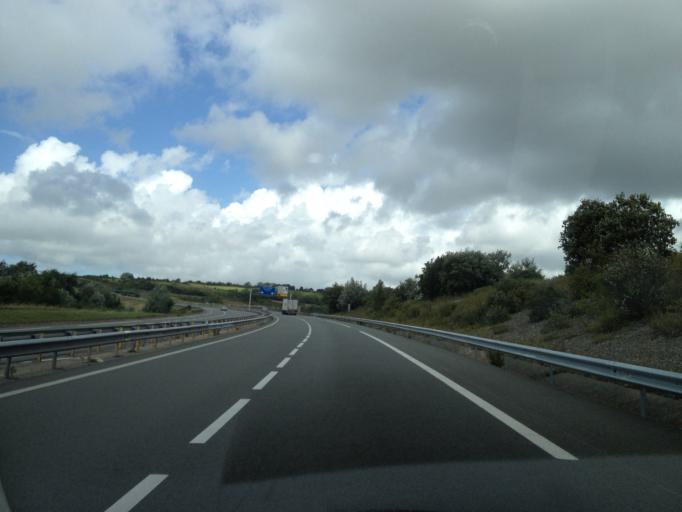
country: FR
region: Nord-Pas-de-Calais
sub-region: Departement du Pas-de-Calais
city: Isques
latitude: 50.6711
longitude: 1.6632
